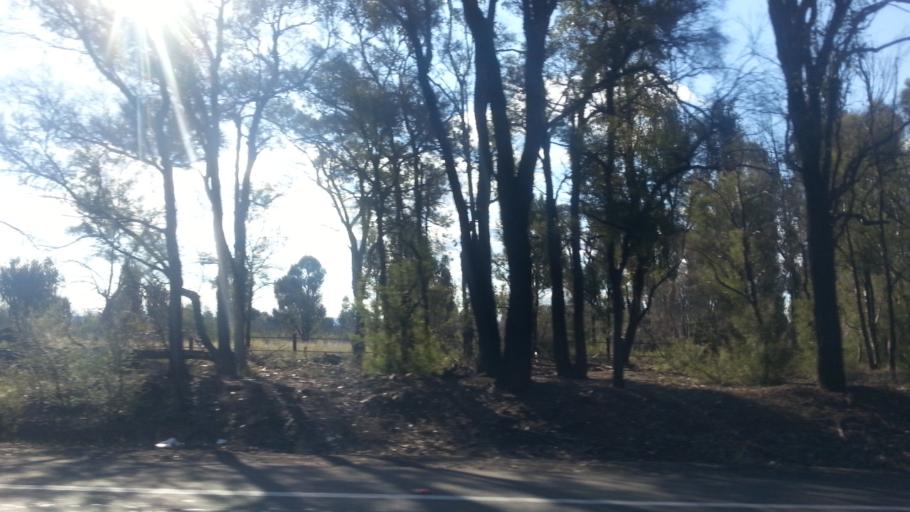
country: AU
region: New South Wales
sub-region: Penrith Municipality
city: Werrington Downs
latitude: -33.7014
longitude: 150.7255
